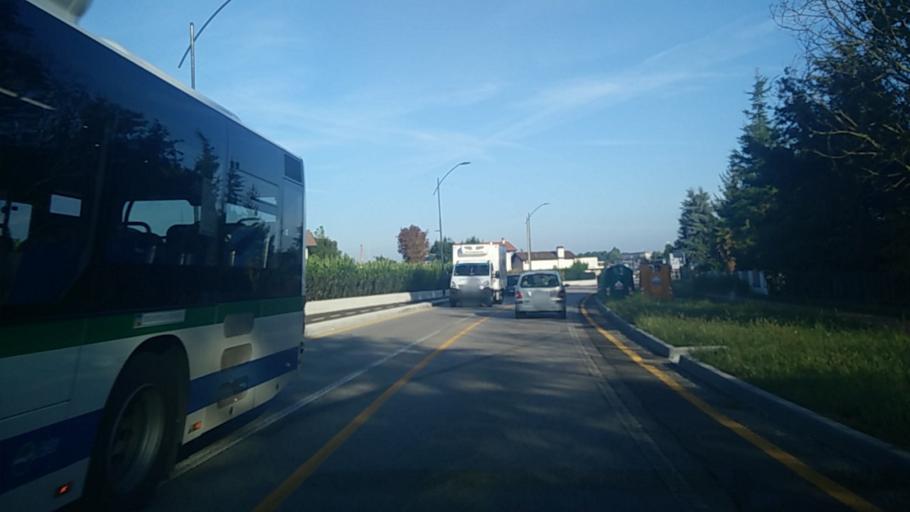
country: IT
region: Veneto
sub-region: Provincia di Venezia
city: Trivignano
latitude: 45.5368
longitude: 12.1766
